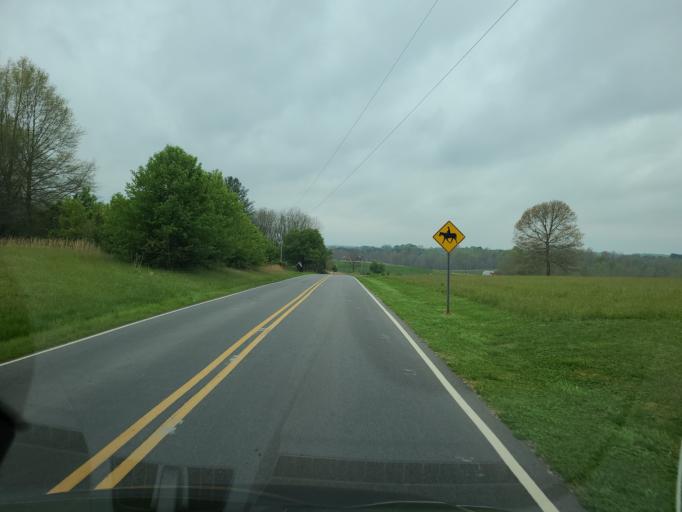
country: US
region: North Carolina
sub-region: Gaston County
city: Cherryville
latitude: 35.4228
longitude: -81.4527
